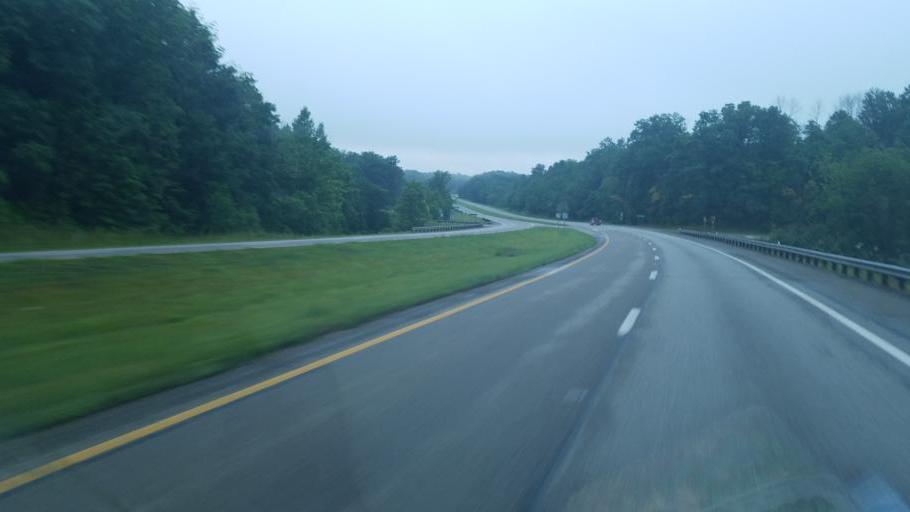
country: US
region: Ohio
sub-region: Jackson County
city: Oak Hill
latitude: 38.9769
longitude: -82.5223
